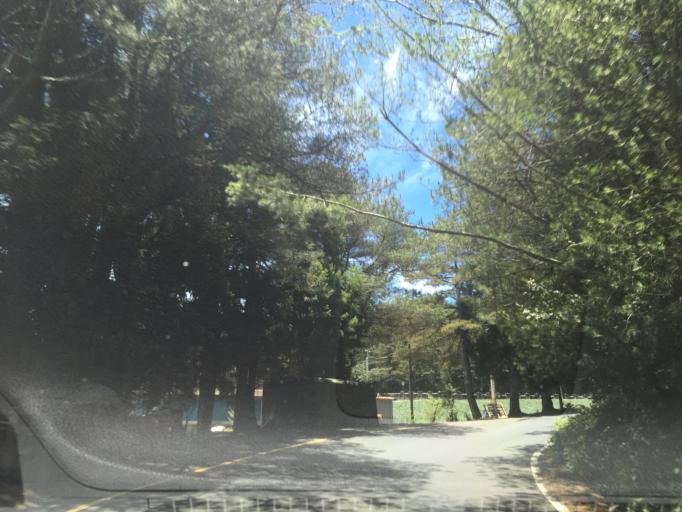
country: TW
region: Taiwan
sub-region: Nantou
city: Puli
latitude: 24.2308
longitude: 121.2443
